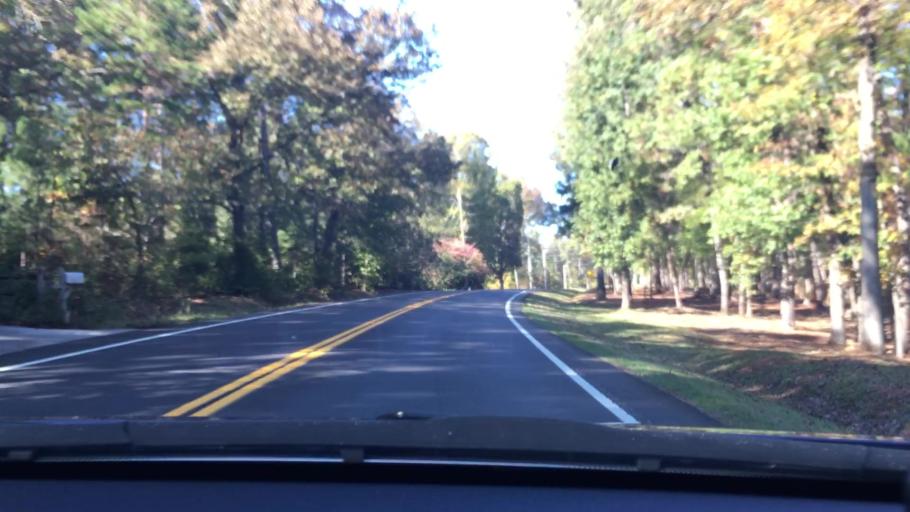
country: US
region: South Carolina
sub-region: Lexington County
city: Irmo
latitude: 34.1280
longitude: -81.1771
